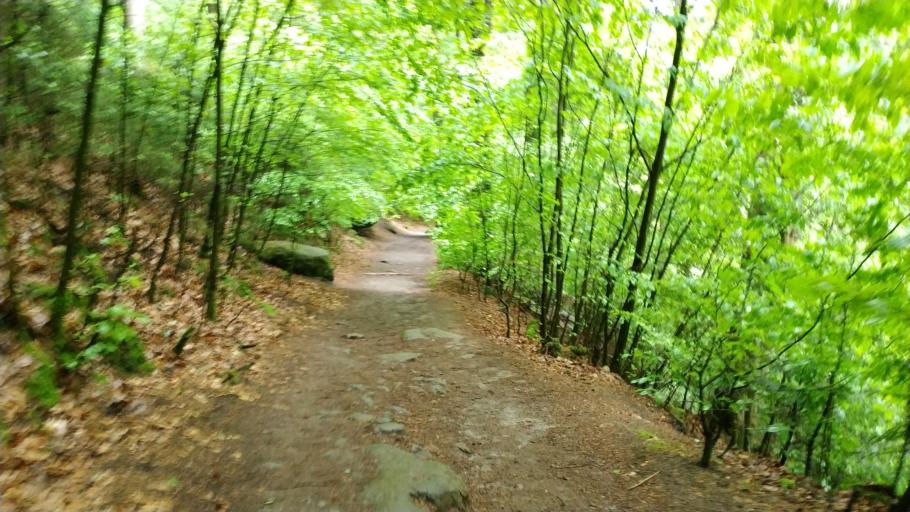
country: DE
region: Saxony
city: Sebnitz
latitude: 50.9281
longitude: 14.2484
